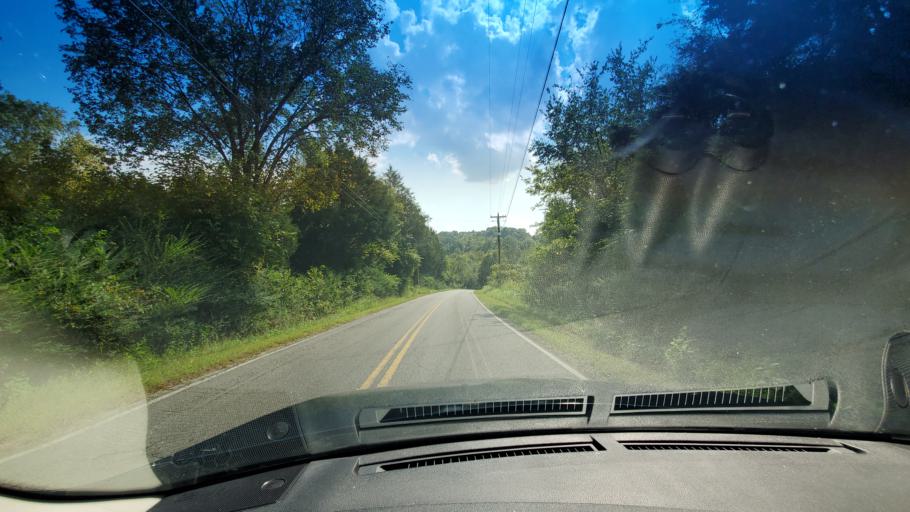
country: US
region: Tennessee
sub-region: Smith County
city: South Carthage
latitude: 36.2420
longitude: -85.9711
